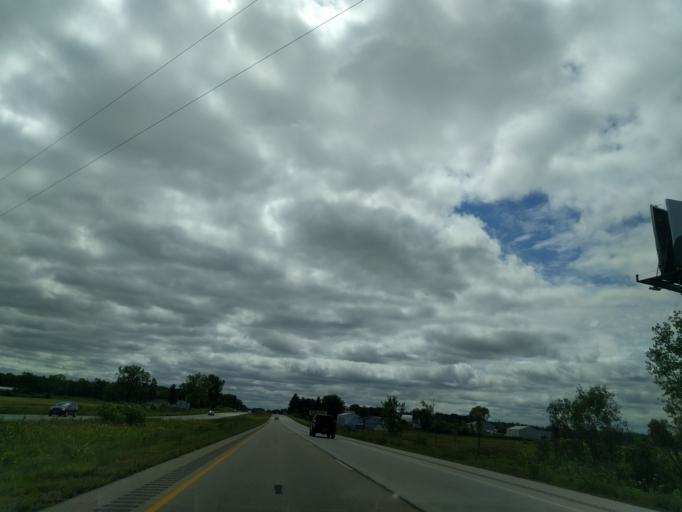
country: US
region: Wisconsin
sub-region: Brown County
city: Suamico
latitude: 44.6603
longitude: -88.0503
